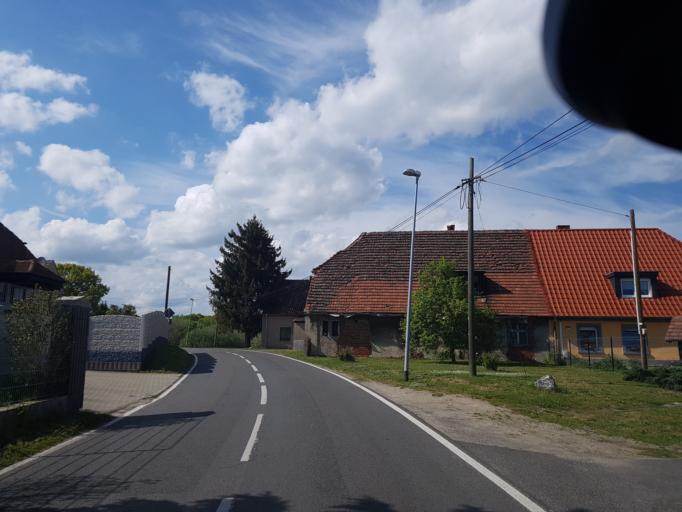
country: DE
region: Brandenburg
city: Spremberg
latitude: 51.6526
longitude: 14.3273
